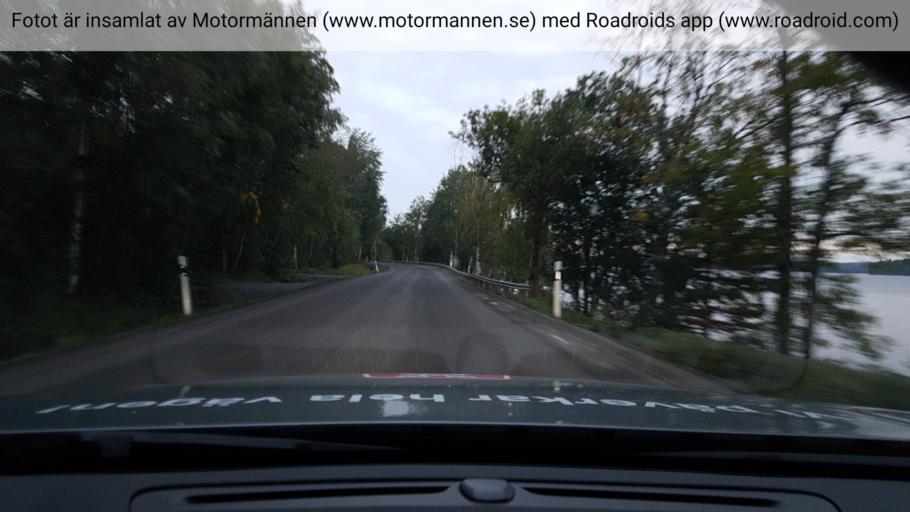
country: SE
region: OErebro
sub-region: Nora Kommun
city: As
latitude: 59.4835
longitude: 14.9248
